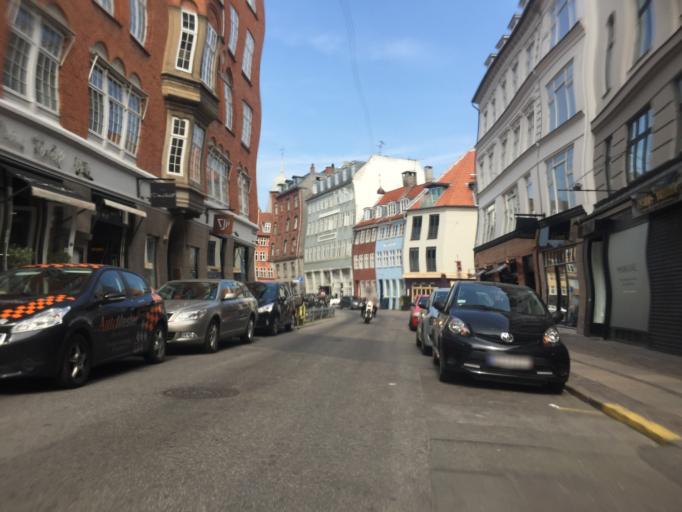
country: DK
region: Capital Region
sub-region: Kobenhavn
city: Christianshavn
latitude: 55.6815
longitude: 12.5818
